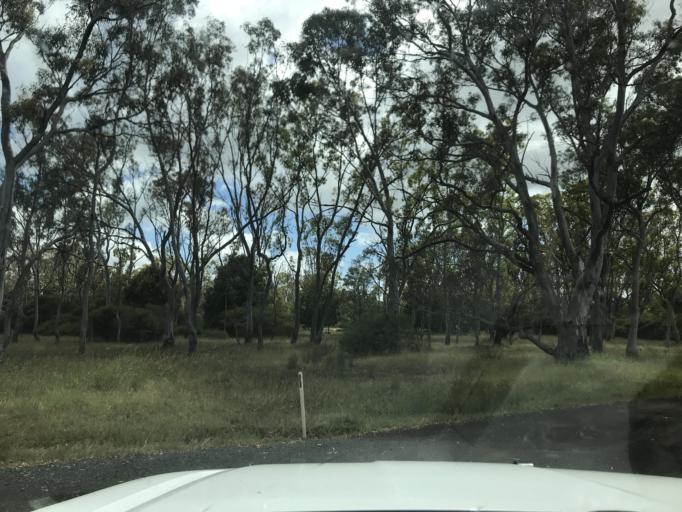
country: AU
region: South Australia
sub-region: Wattle Range
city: Penola
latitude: -37.1815
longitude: 141.4424
